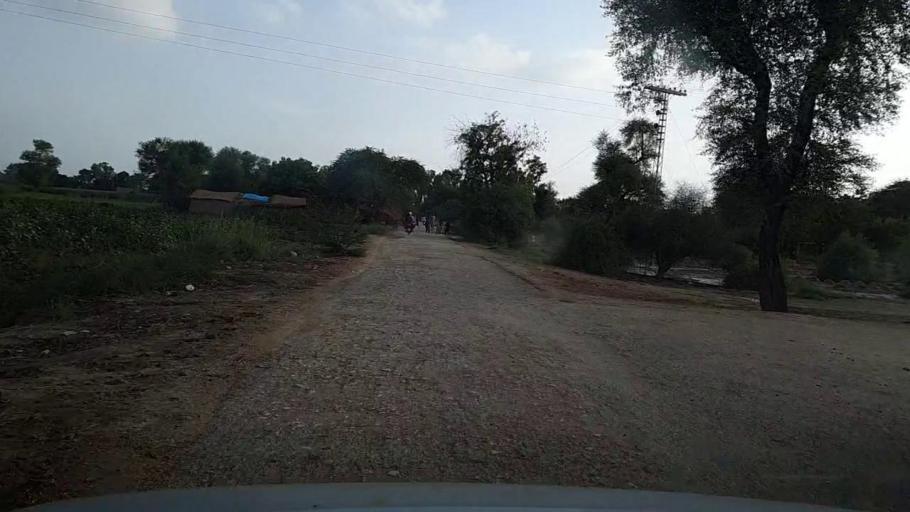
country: PK
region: Sindh
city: Pad Idan
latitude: 26.7907
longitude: 68.2227
